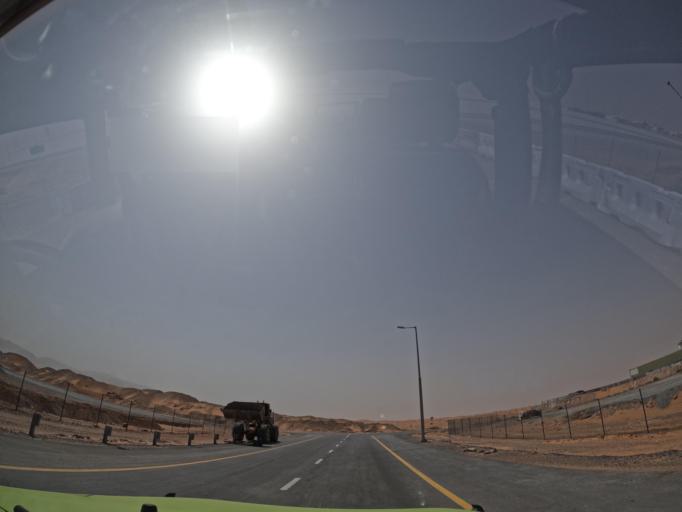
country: OM
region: Al Buraimi
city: Al Buraymi
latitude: 24.7396
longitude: 55.7979
